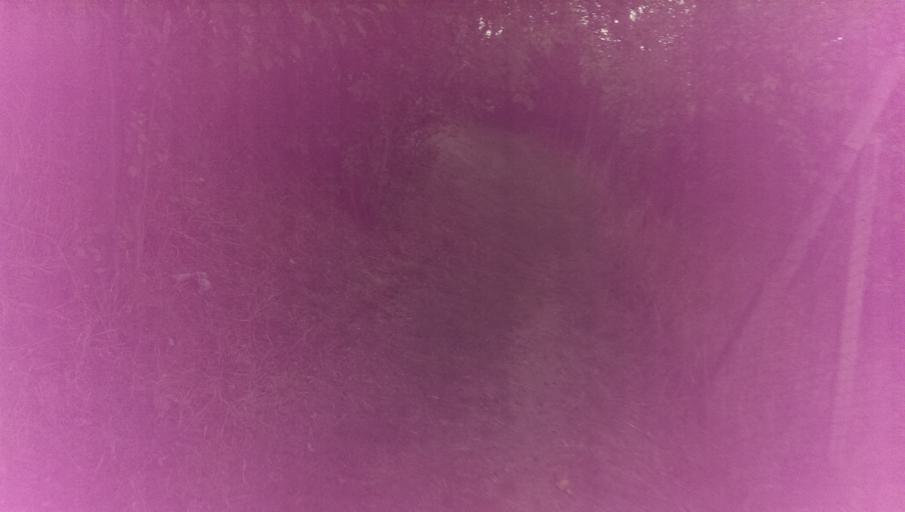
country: CZ
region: Zlin
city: Kunovice
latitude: 49.0536
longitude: 17.4808
